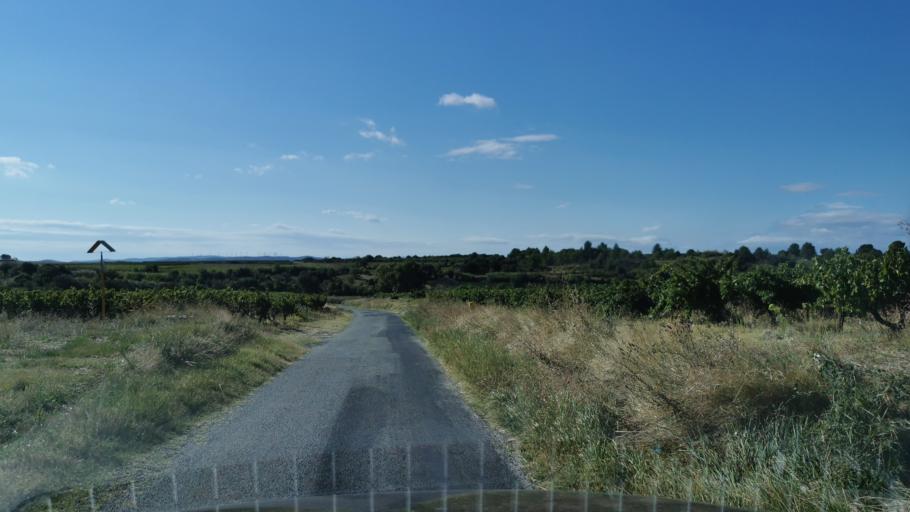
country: FR
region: Languedoc-Roussillon
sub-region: Departement de l'Aude
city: Ginestas
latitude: 43.2663
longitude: 2.8434
